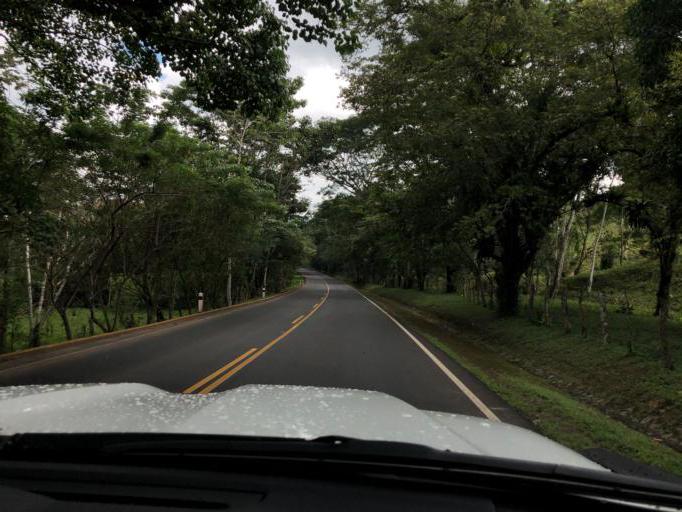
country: NI
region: Chontales
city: Villa Sandino
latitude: 11.9978
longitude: -84.8846
